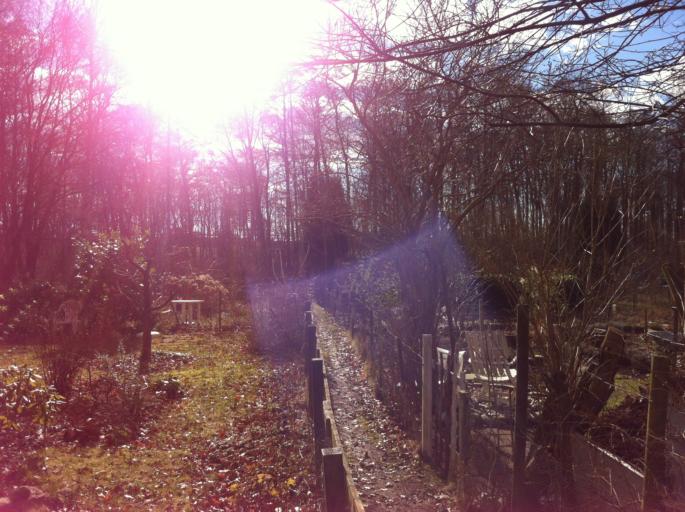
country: SE
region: Skane
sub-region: Helsingborg
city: Rydeback
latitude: 56.0104
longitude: 12.7521
